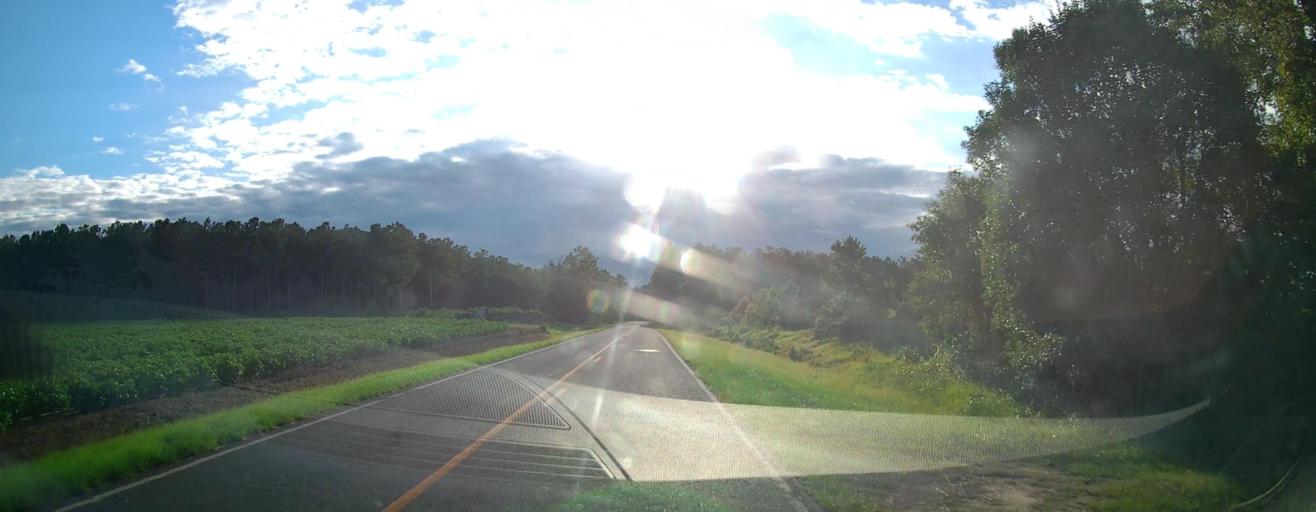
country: US
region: Georgia
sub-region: Pulaski County
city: Hawkinsville
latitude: 32.2877
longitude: -83.5482
